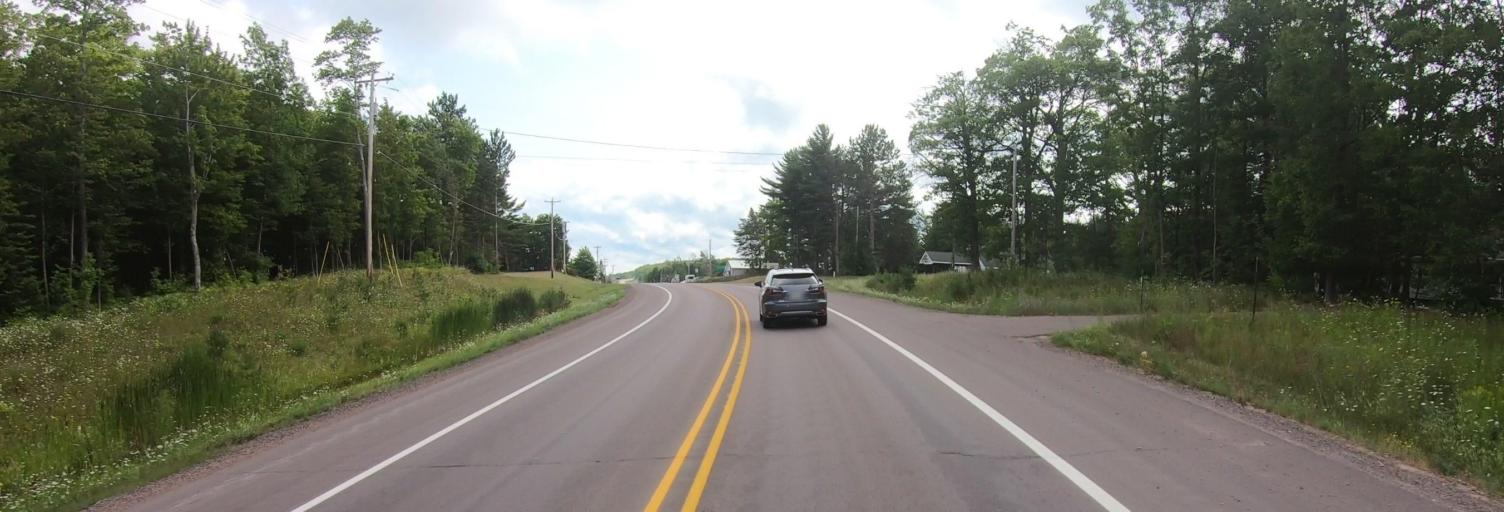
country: US
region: Michigan
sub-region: Houghton County
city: Hancock
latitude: 47.0780
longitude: -88.6405
